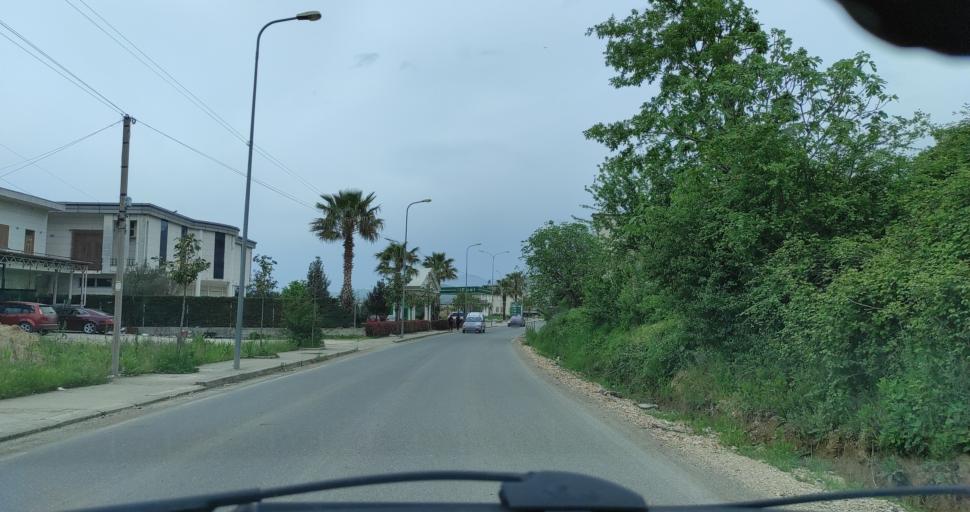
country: AL
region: Lezhe
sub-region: Rrethi i Kurbinit
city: Lac
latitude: 41.6236
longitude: 19.7085
